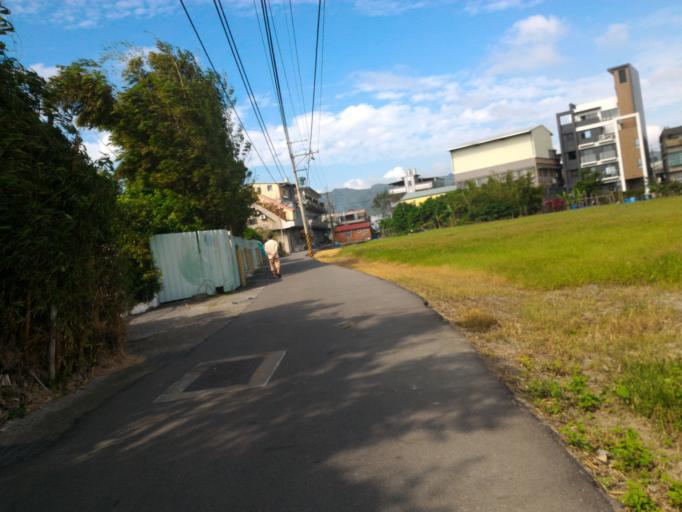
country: TW
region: Taiwan
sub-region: Taoyuan
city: Taoyuan
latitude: 24.9550
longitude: 121.3930
